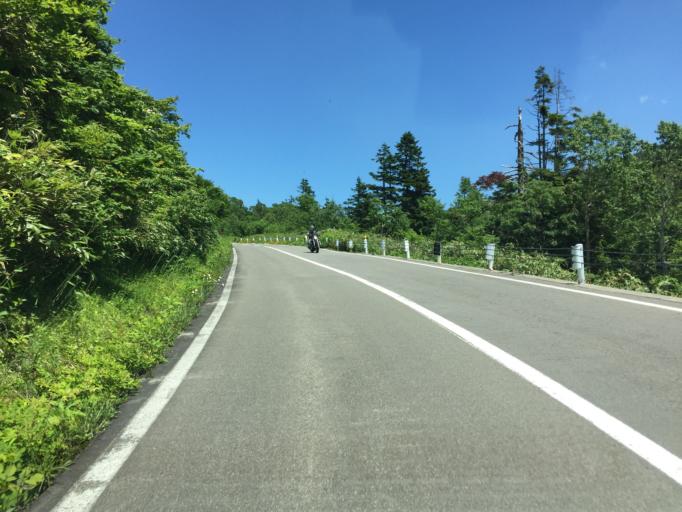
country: JP
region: Fukushima
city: Inawashiro
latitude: 37.6937
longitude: 140.2471
